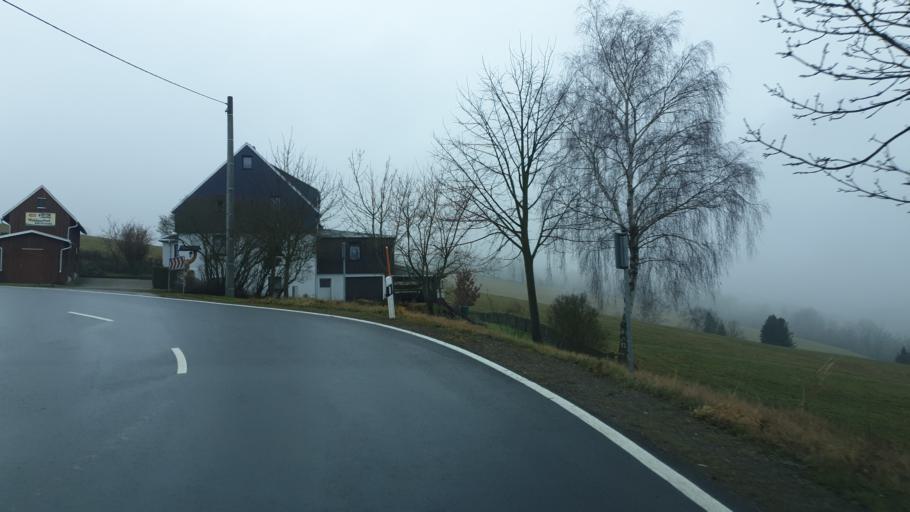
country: DE
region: Saxony
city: Neuhausen
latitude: 50.6717
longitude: 13.4720
